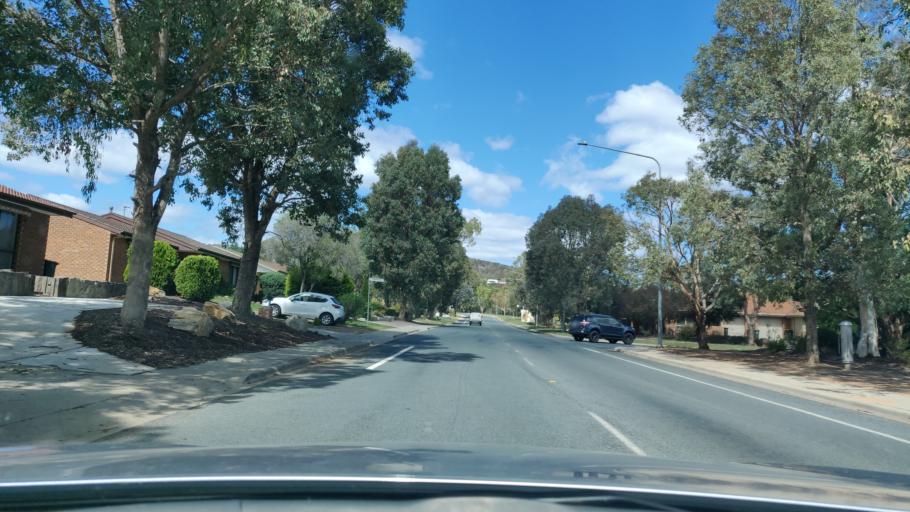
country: AU
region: Australian Capital Territory
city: Macarthur
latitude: -35.4380
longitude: 149.0979
